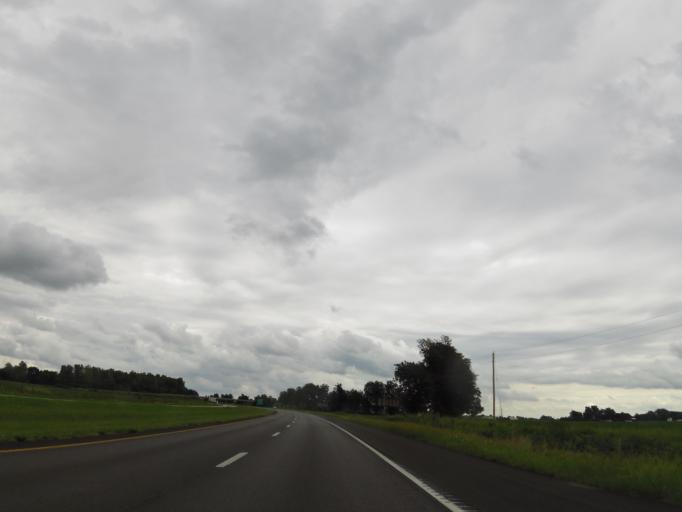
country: US
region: Missouri
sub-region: Mississippi County
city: Charleston
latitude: 36.9062
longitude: -89.3396
